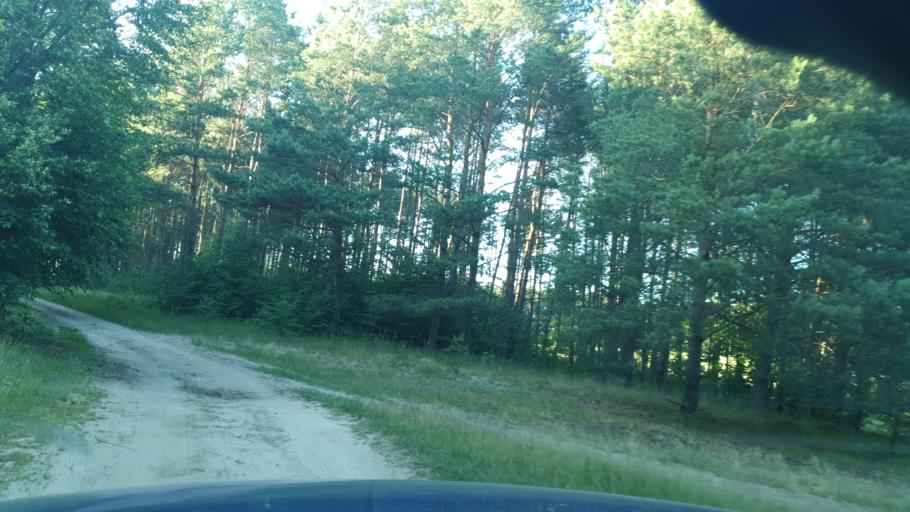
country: PL
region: Pomeranian Voivodeship
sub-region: Powiat bytowski
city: Lipnica
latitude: 53.8796
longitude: 17.4276
